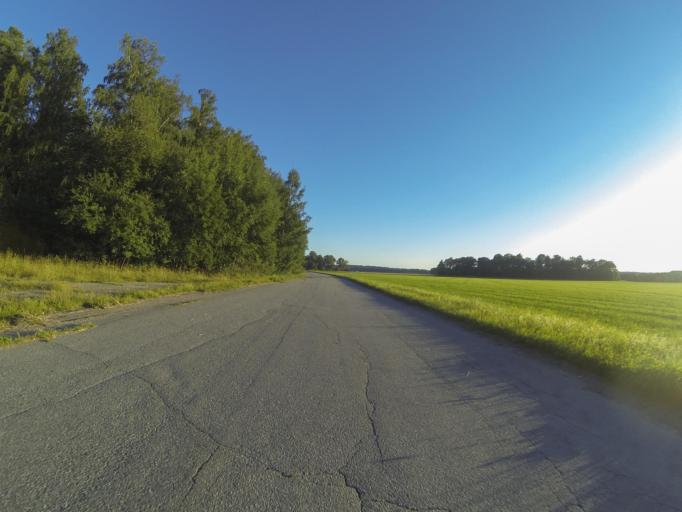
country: SE
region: Vaestmanland
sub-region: Vasteras
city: Vasteras
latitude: 59.5758
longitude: 16.6542
